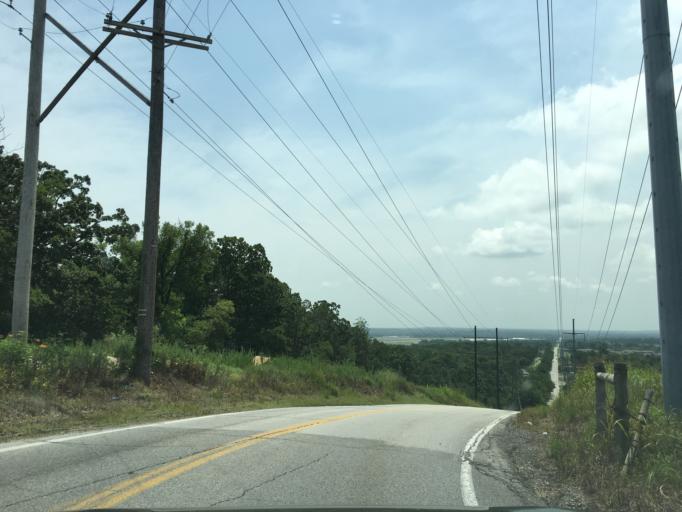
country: US
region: Oklahoma
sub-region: Tulsa County
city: Jenks
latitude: 36.0703
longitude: -95.9939
